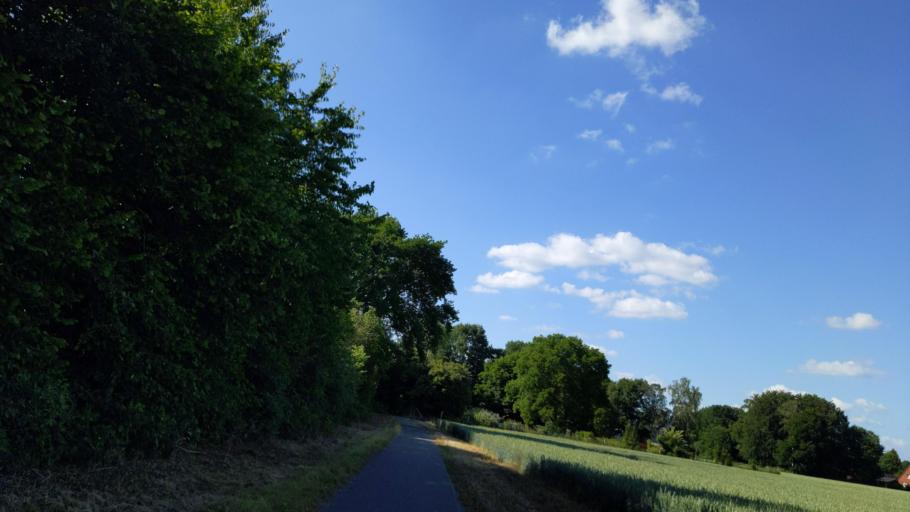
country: DE
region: Schleswig-Holstein
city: Klempau
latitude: 53.7587
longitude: 10.6580
